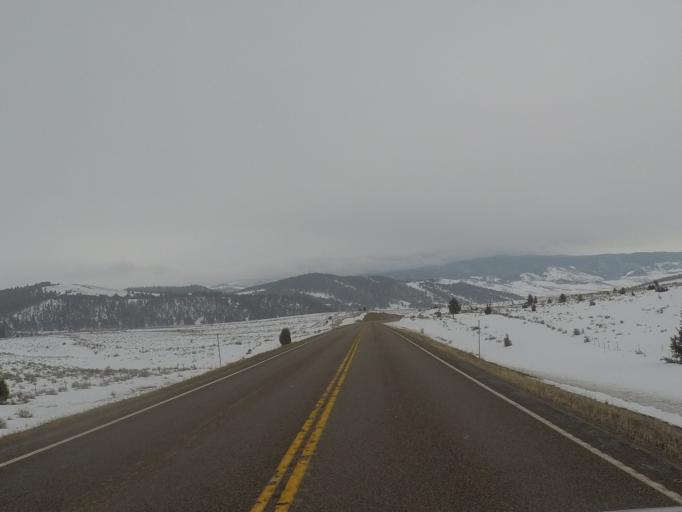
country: US
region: Montana
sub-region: Meagher County
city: White Sulphur Springs
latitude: 46.6335
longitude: -110.8533
